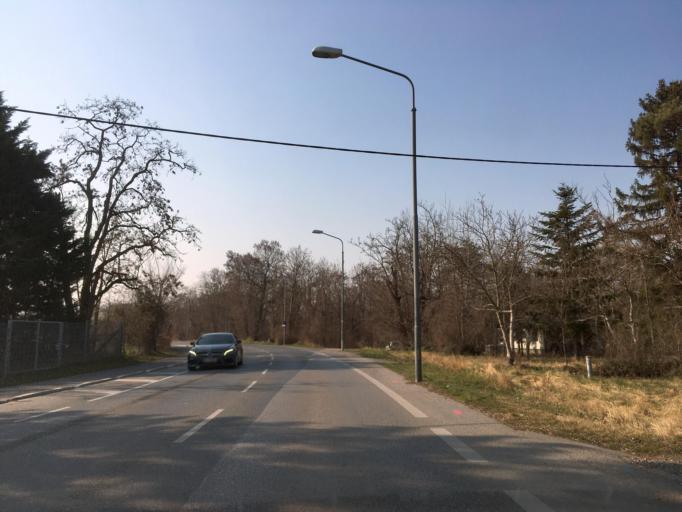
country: AT
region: Lower Austria
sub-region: Politischer Bezirk Wien-Umgebung
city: Schwechat
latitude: 48.1976
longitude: 16.4673
